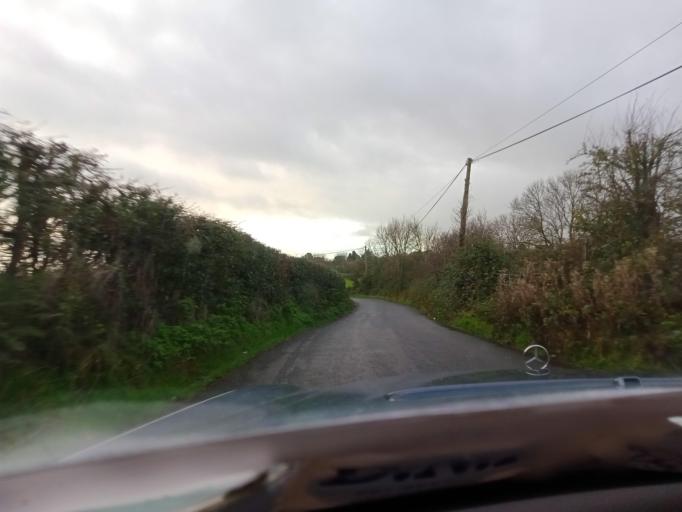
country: IE
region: Munster
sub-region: Waterford
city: Waterford
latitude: 52.2760
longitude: -7.1788
